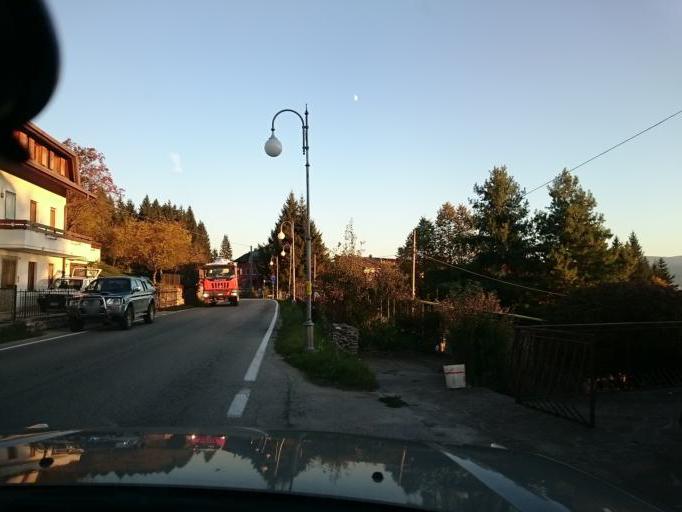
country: IT
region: Veneto
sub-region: Provincia di Vicenza
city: Canove di Roana
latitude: 45.8838
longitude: 11.4771
